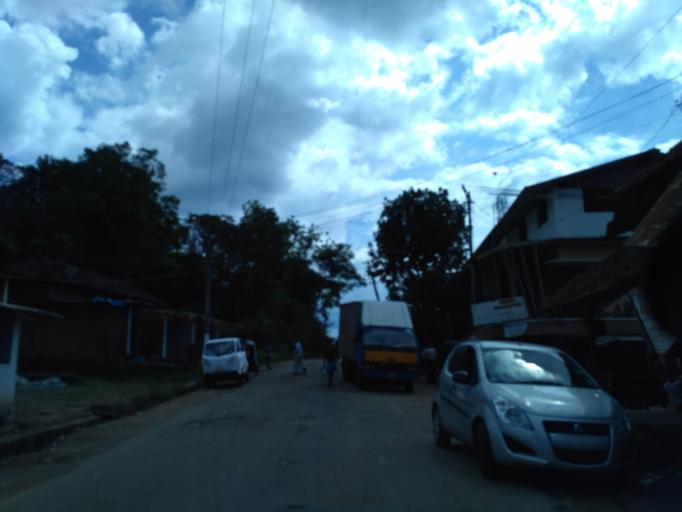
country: IN
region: Karnataka
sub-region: Kodagu
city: Madikeri
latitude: 12.3645
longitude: 75.6956
